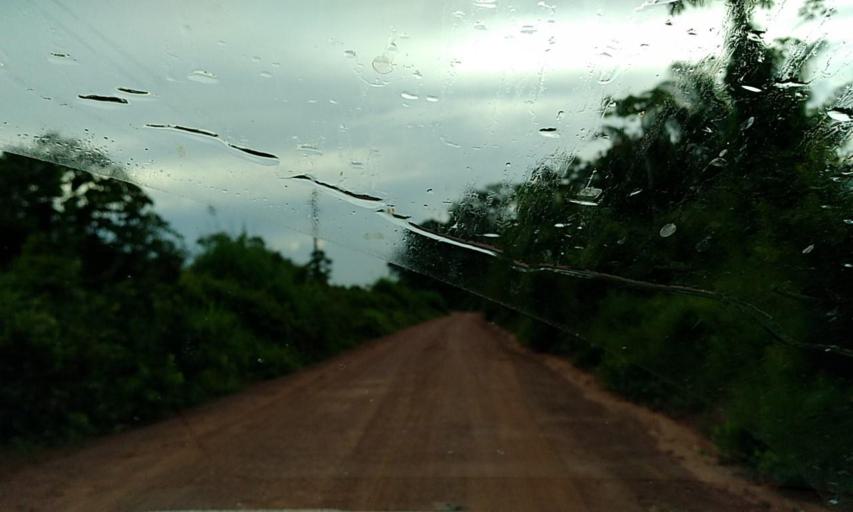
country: BR
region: Para
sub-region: Senador Jose Porfirio
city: Senador Jose Porfirio
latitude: -2.5532
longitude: -51.8675
